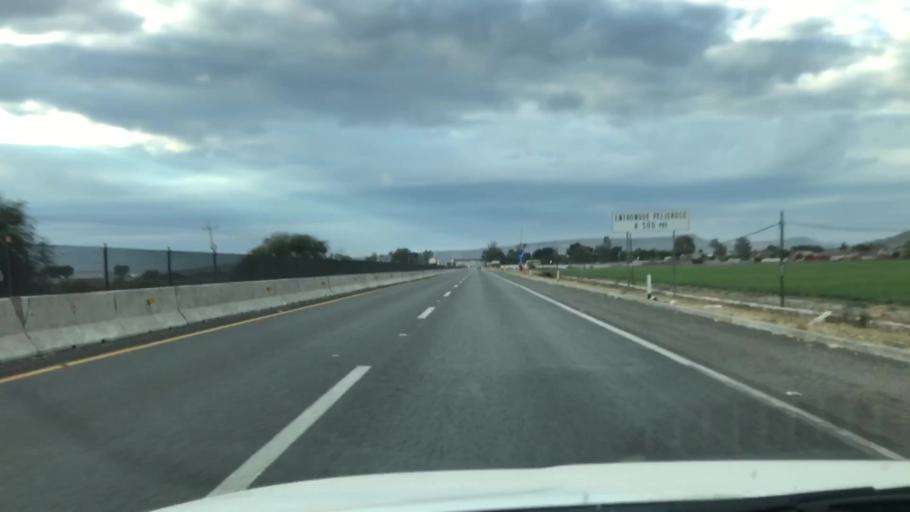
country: MX
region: Guanajuato
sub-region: Penjamo
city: Estacion la Piedad
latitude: 20.3868
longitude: -101.9146
